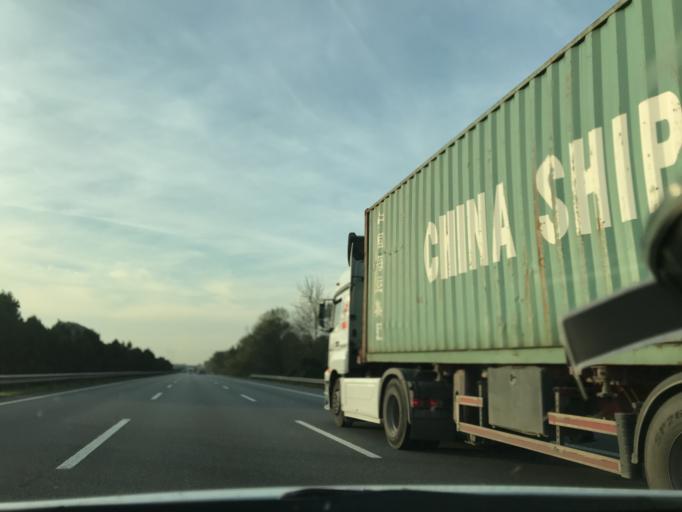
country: TR
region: Duzce
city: Cilimli
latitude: 40.8224
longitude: 31.0656
